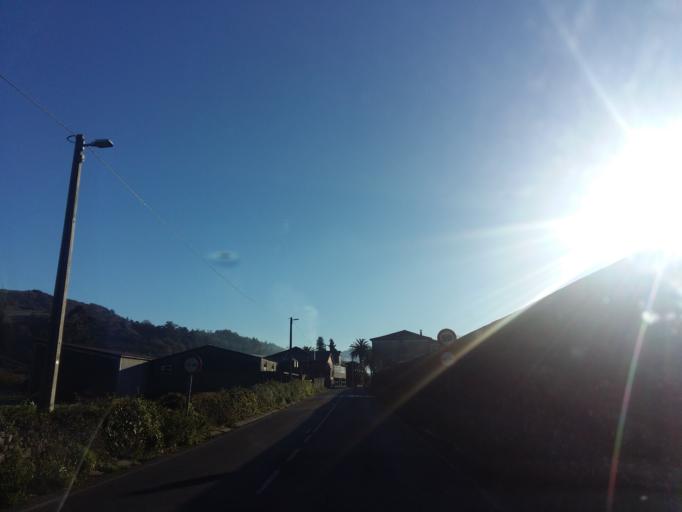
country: ES
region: Cantabria
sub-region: Provincia de Cantabria
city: Ramales de la Victoria
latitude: 43.2796
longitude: -3.5295
